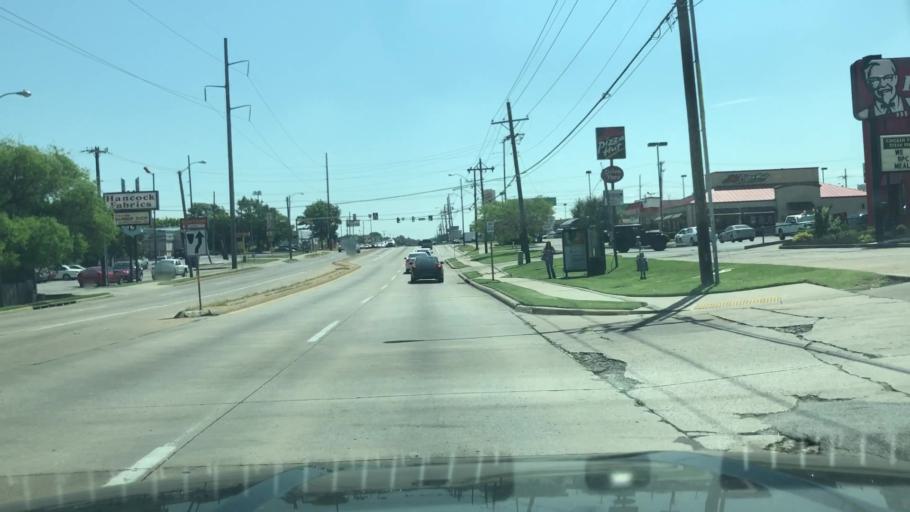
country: US
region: Oklahoma
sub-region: Tulsa County
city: Broken Arrow
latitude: 36.1334
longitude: -95.8531
